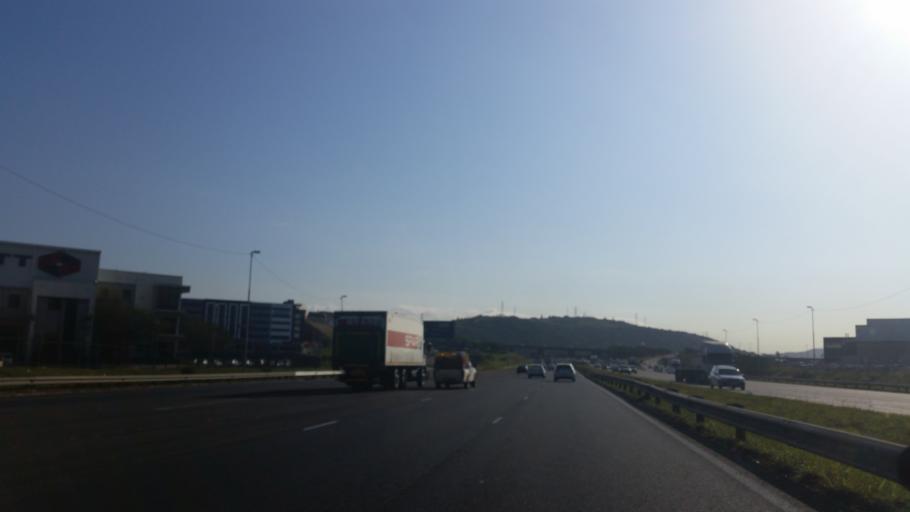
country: ZA
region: KwaZulu-Natal
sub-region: eThekwini Metropolitan Municipality
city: Berea
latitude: -29.7819
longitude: 30.9974
